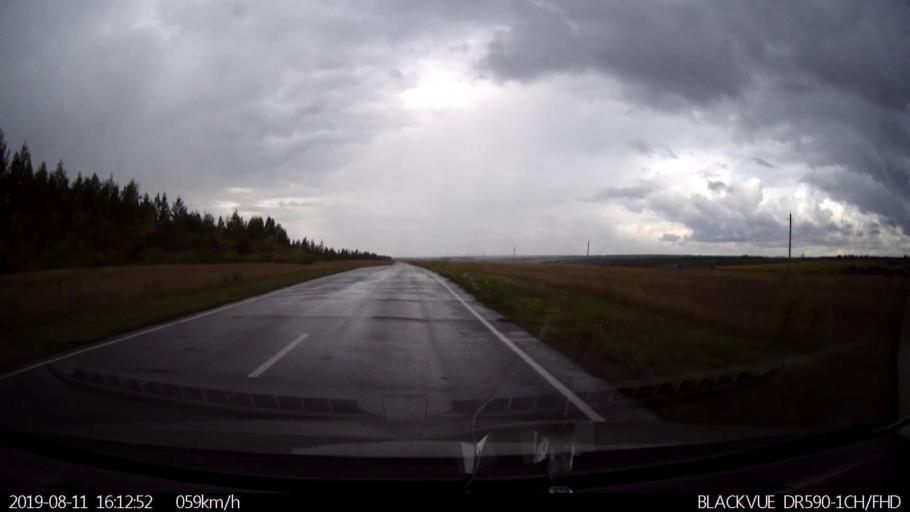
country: RU
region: Ulyanovsk
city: Ignatovka
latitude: 54.0152
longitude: 47.6390
